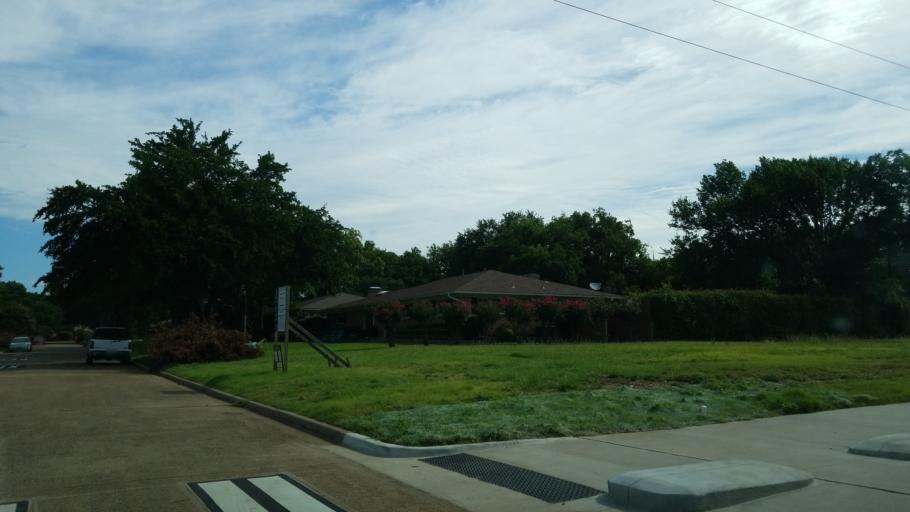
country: US
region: Texas
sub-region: Dallas County
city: Farmers Branch
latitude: 32.8996
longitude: -96.8396
